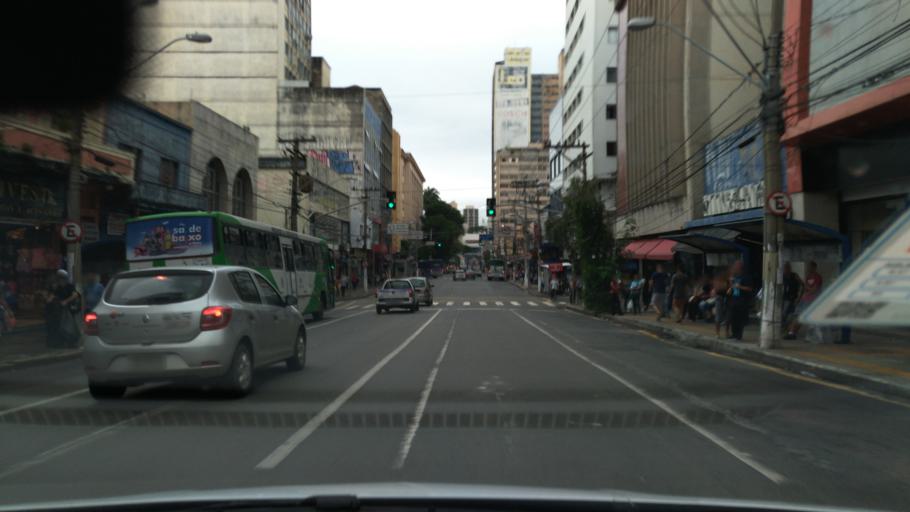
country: BR
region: Sao Paulo
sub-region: Campinas
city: Campinas
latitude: -22.9056
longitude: -47.0626
